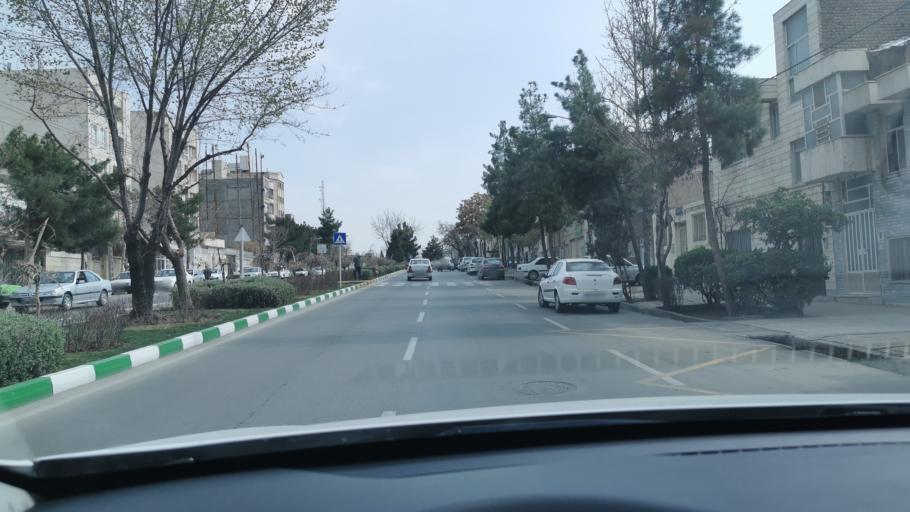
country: IR
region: Razavi Khorasan
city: Mashhad
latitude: 36.2762
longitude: 59.5664
